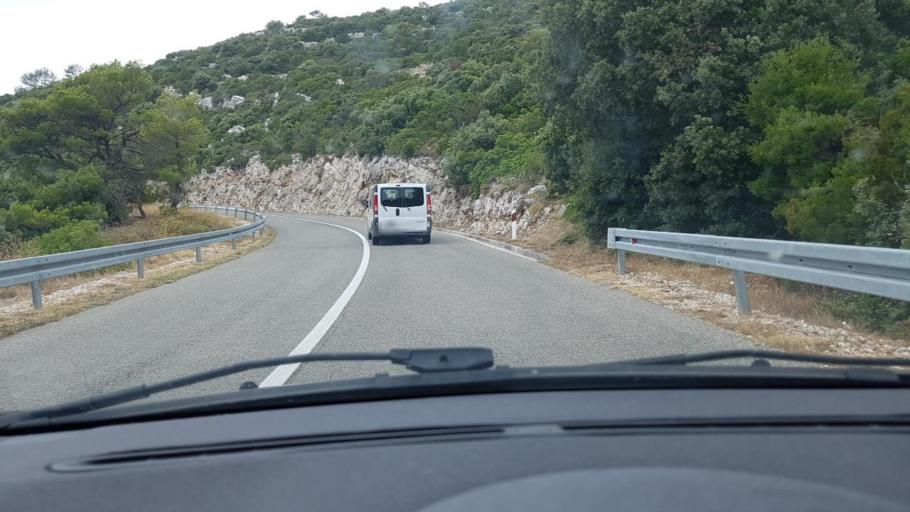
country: HR
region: Dubrovacko-Neretvanska
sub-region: Grad Korcula
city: Zrnovo
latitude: 42.9391
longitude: 17.0190
